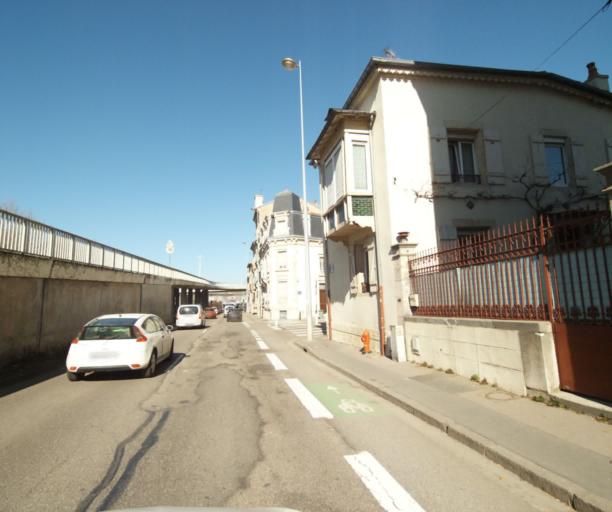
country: FR
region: Lorraine
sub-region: Departement de Meurthe-et-Moselle
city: Malzeville
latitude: 48.6999
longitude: 6.1871
